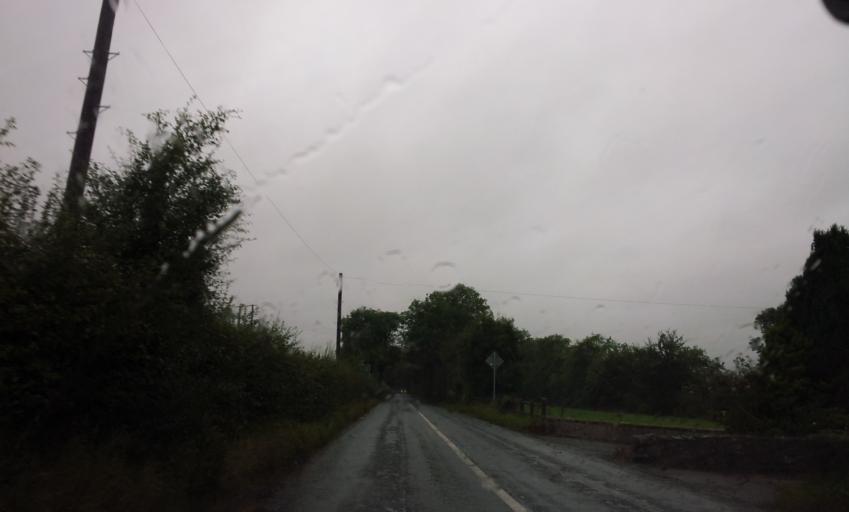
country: IE
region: Munster
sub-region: County Cork
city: Mallow
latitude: 52.1490
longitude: -8.6170
